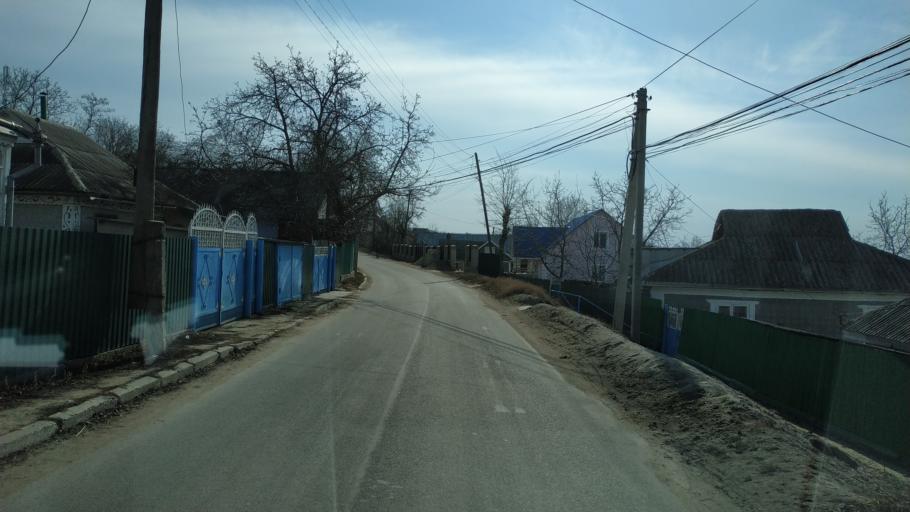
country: MD
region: Nisporeni
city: Nisporeni
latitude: 47.1736
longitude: 28.1288
